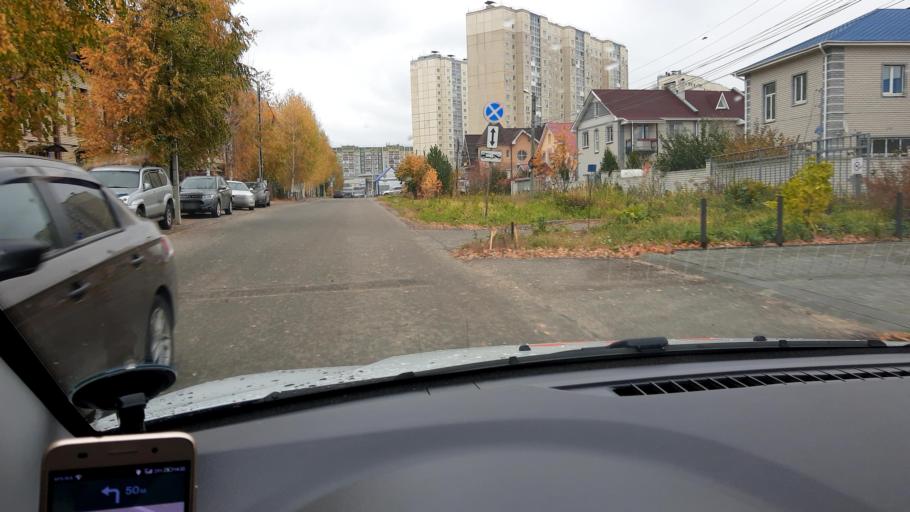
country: RU
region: Nizjnij Novgorod
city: Afonino
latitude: 56.2827
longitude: 44.0645
